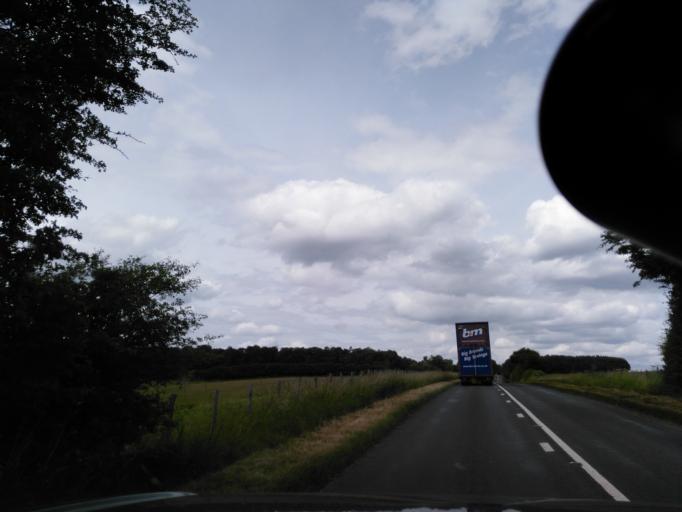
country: GB
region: England
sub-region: Wiltshire
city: Woodford
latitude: 51.1440
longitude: -1.8588
